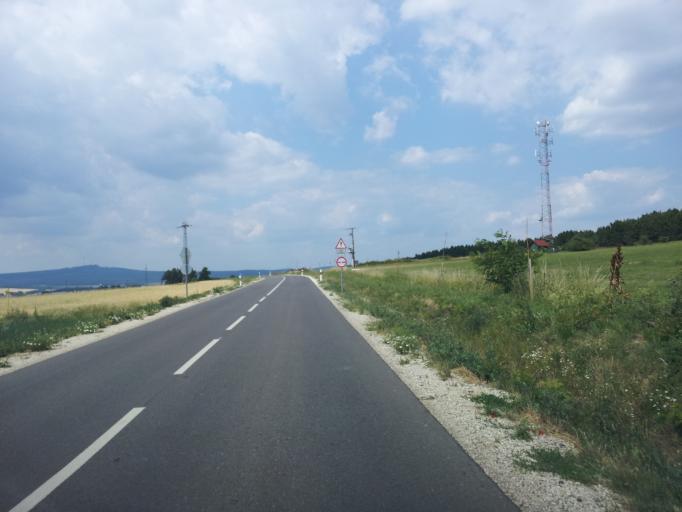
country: HU
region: Veszprem
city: Zanka
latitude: 46.9558
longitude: 17.7020
